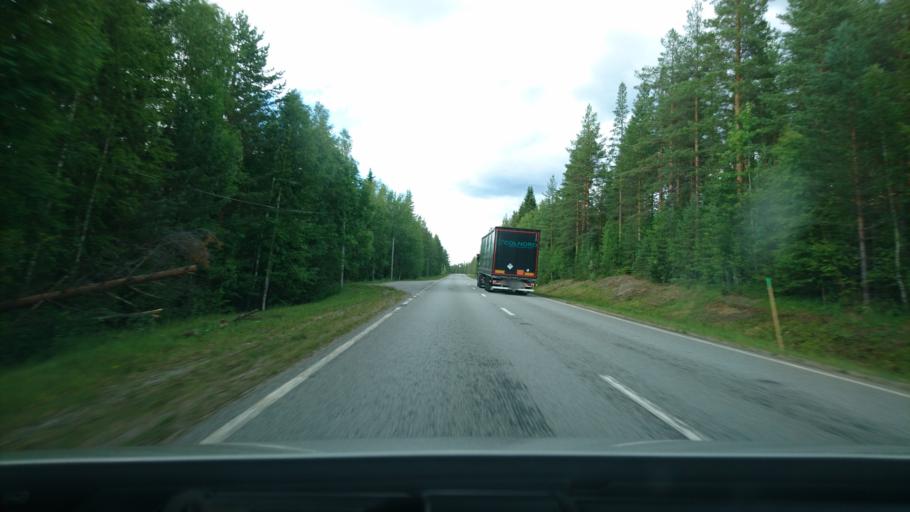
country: SE
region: Vaesterbotten
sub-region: Asele Kommun
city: Asele
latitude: 63.8496
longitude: 17.1590
